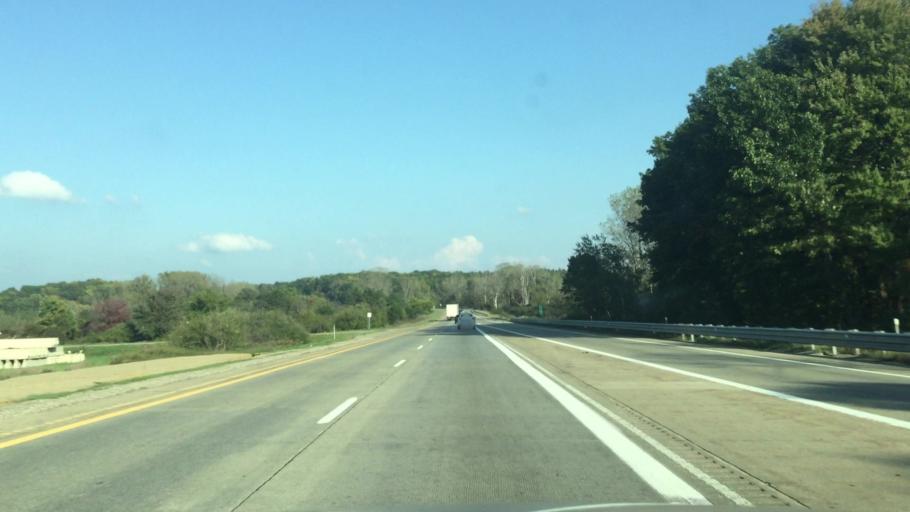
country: US
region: Michigan
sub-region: Jackson County
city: Michigan Center
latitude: 42.2805
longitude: -84.3019
